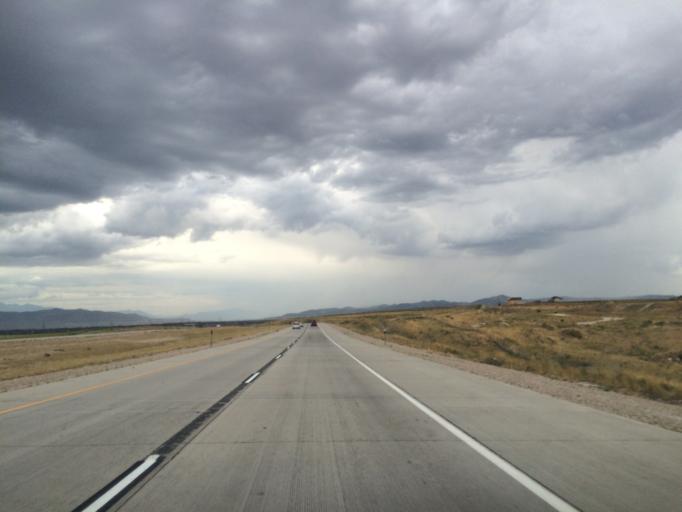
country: US
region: Utah
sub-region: Salt Lake County
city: Oquirrh
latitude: 40.6219
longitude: -112.0440
